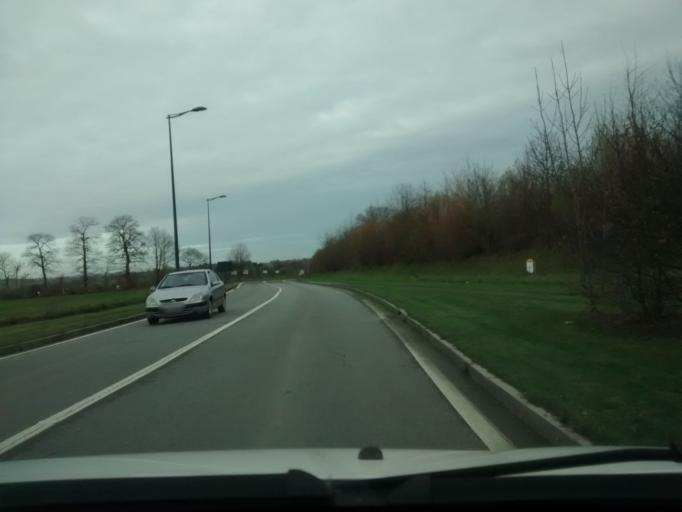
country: FR
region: Brittany
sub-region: Departement d'Ille-et-Vilaine
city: Vitre
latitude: 48.1127
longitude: -1.2243
